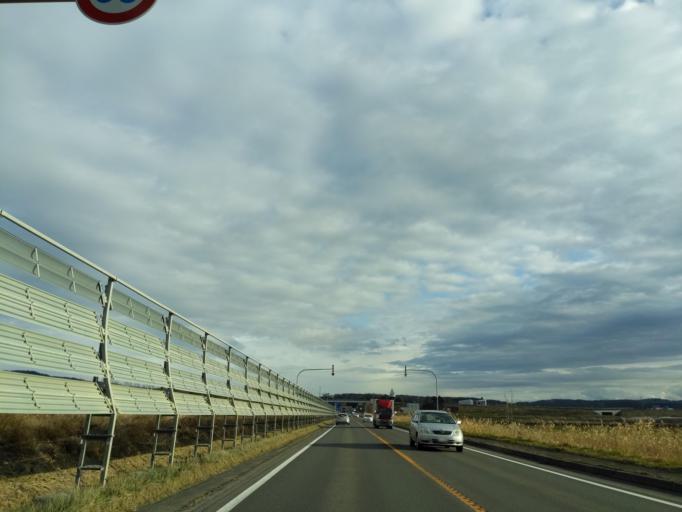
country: JP
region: Hokkaido
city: Kitahiroshima
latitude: 42.9530
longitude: 141.7093
